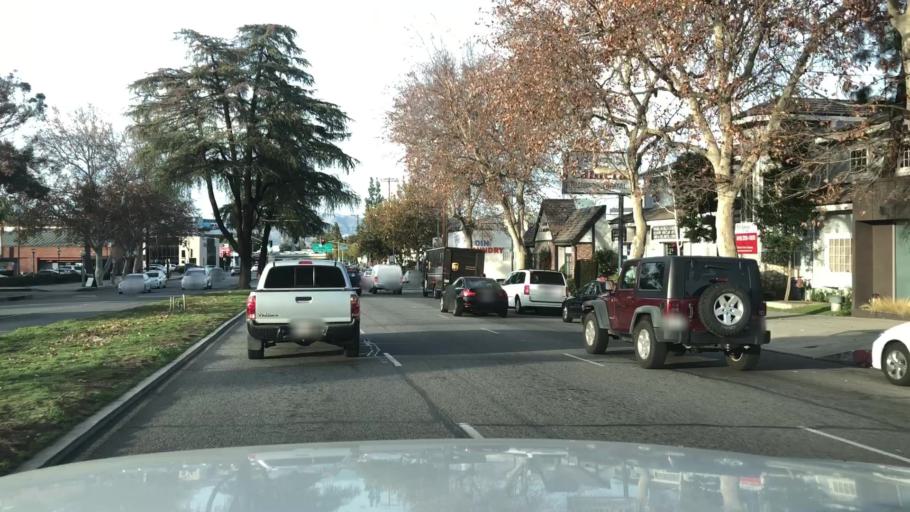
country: US
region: California
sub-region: Los Angeles County
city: Woodland Hills
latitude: 34.1669
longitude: -118.6058
